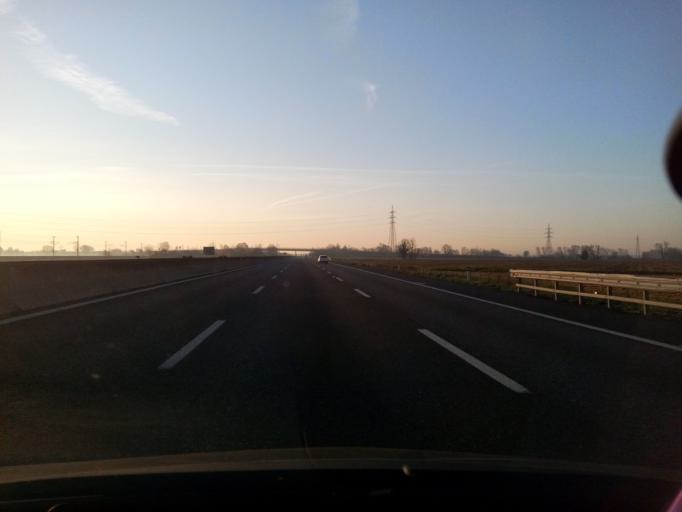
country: IT
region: Lombardy
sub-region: Provincia di Lodi
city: Salerano sul Lambro
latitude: 45.3115
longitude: 9.3912
